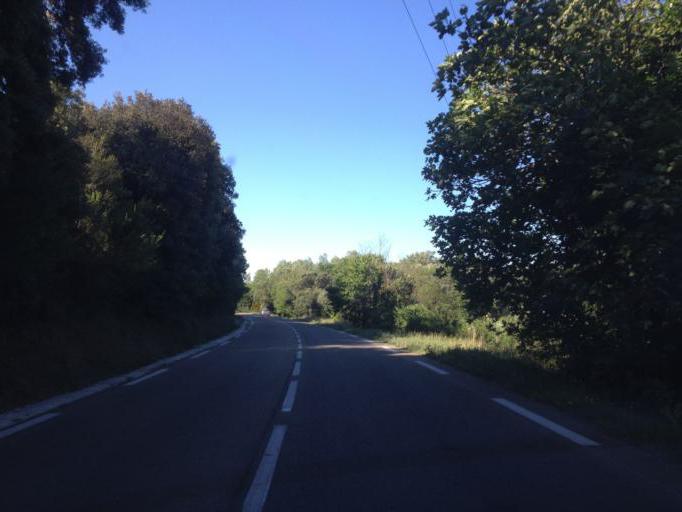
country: FR
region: Languedoc-Roussillon
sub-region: Departement du Gard
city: Montfaucon
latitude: 44.0846
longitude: 4.7778
